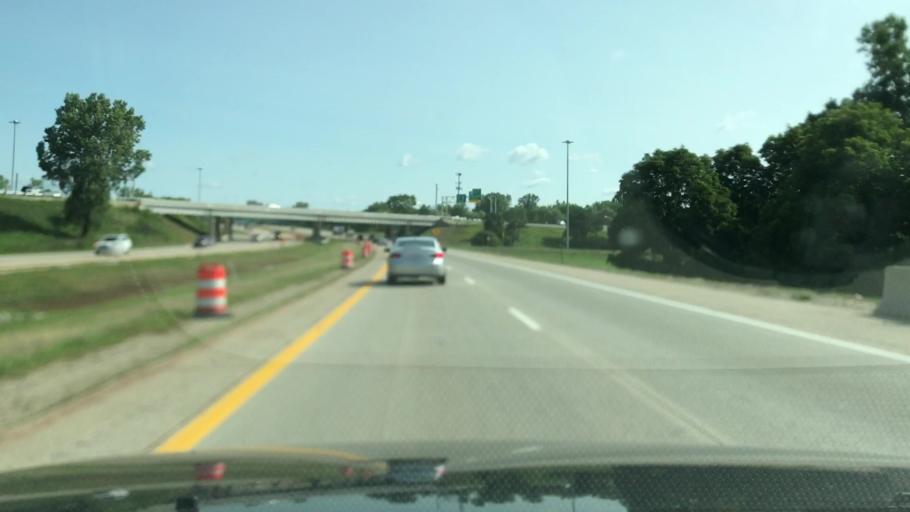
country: US
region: Michigan
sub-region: Kent County
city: Comstock Park
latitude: 43.0191
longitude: -85.6697
